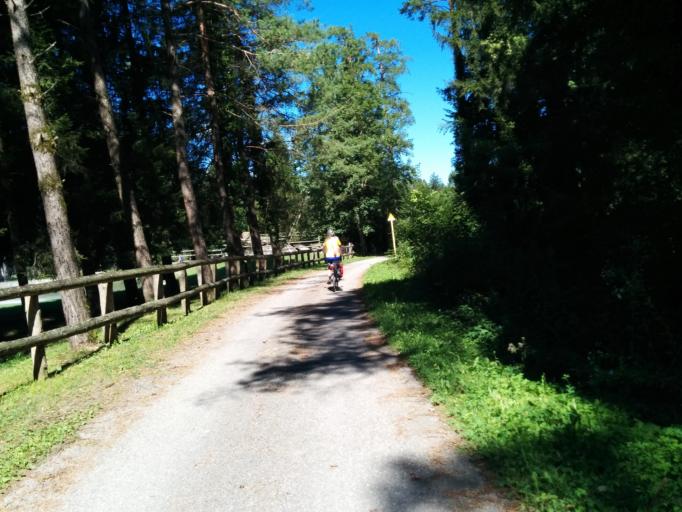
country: IT
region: Friuli Venezia Giulia
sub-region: Provincia di Udine
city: Villa Santina
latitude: 46.4090
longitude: 12.9143
